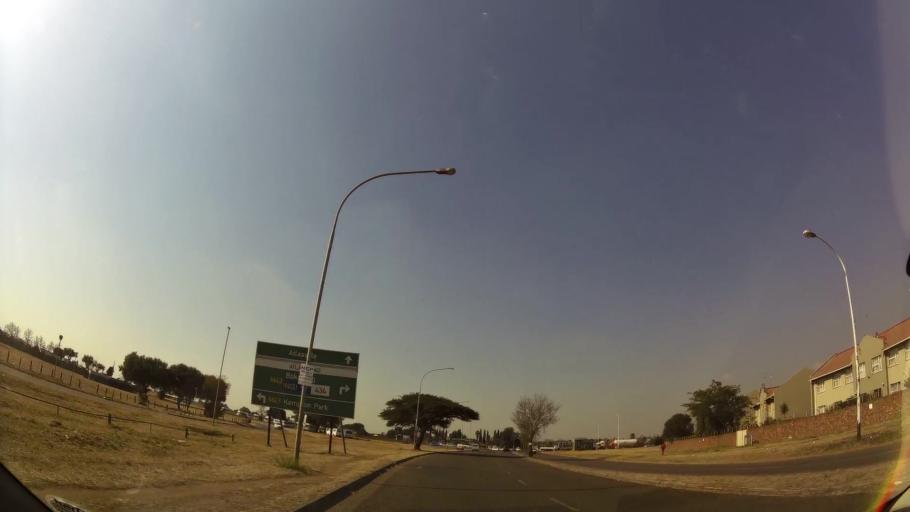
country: ZA
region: Gauteng
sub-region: Ekurhuleni Metropolitan Municipality
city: Benoni
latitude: -26.1602
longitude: 28.2754
